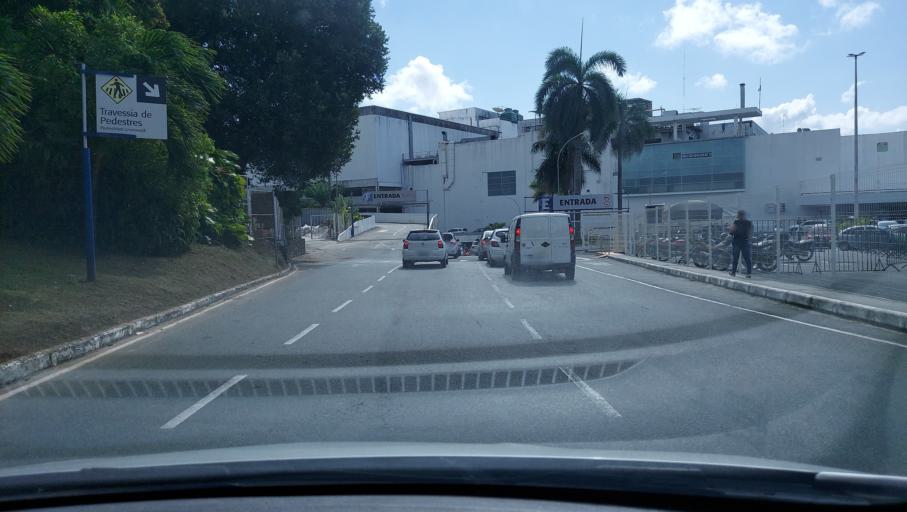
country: BR
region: Bahia
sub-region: Salvador
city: Salvador
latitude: -12.9823
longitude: -38.4621
